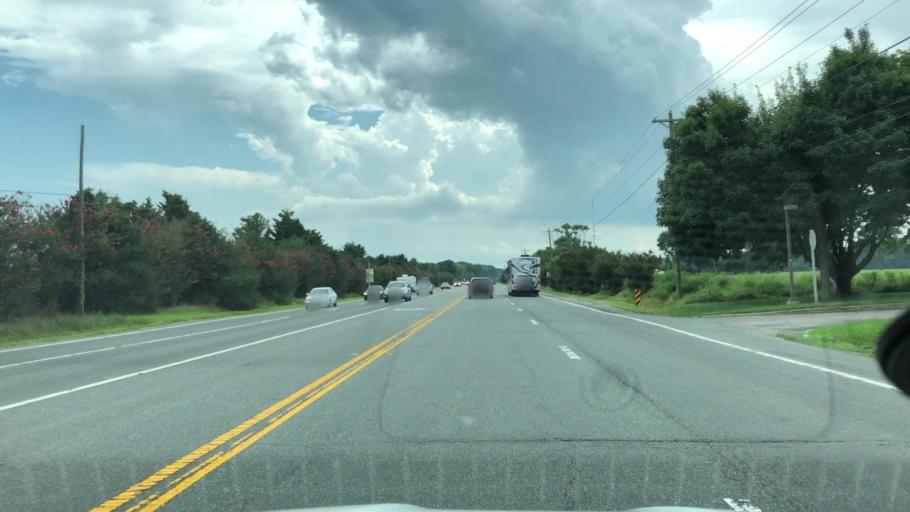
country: US
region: Virginia
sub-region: Accomack County
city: Wattsville
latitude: 37.8541
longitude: -75.5621
